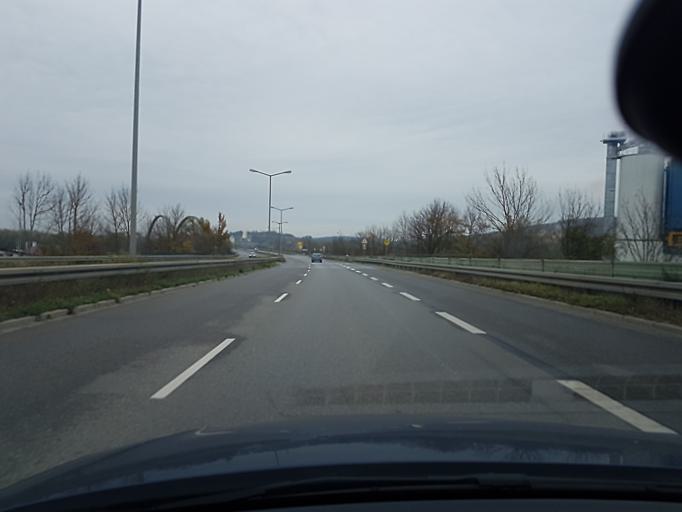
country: DE
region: Bavaria
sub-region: Upper Palatinate
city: Regensburg
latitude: 49.0175
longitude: 12.1436
